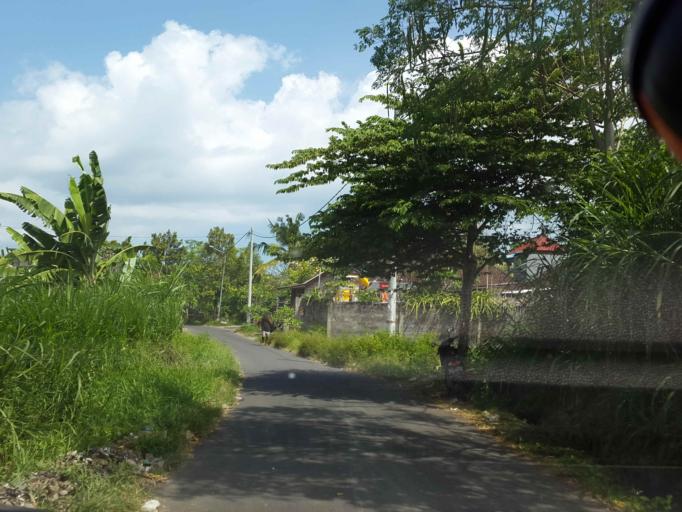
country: ID
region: Bali
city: Klungkung
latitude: -8.5536
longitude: 115.3785
